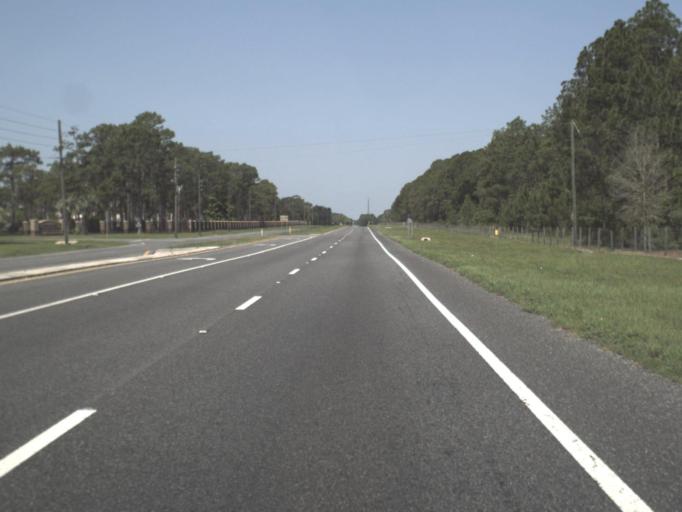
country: US
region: Florida
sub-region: Bradford County
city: Starke
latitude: 29.9818
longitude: -81.9828
